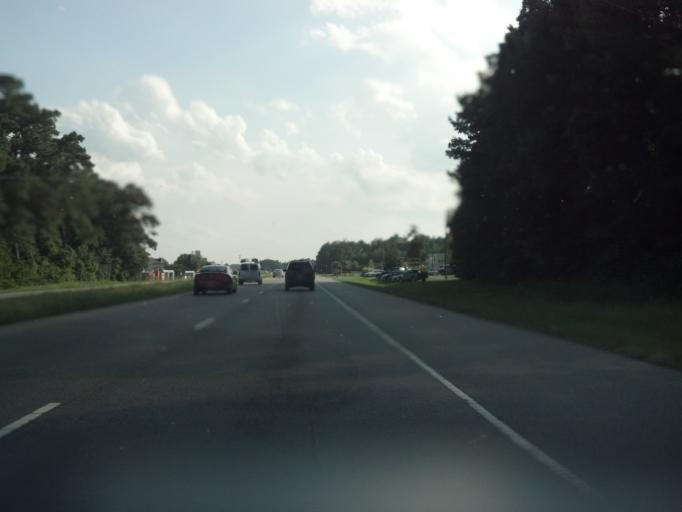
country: US
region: North Carolina
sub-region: Pitt County
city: Greenville
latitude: 35.6474
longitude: -77.3678
